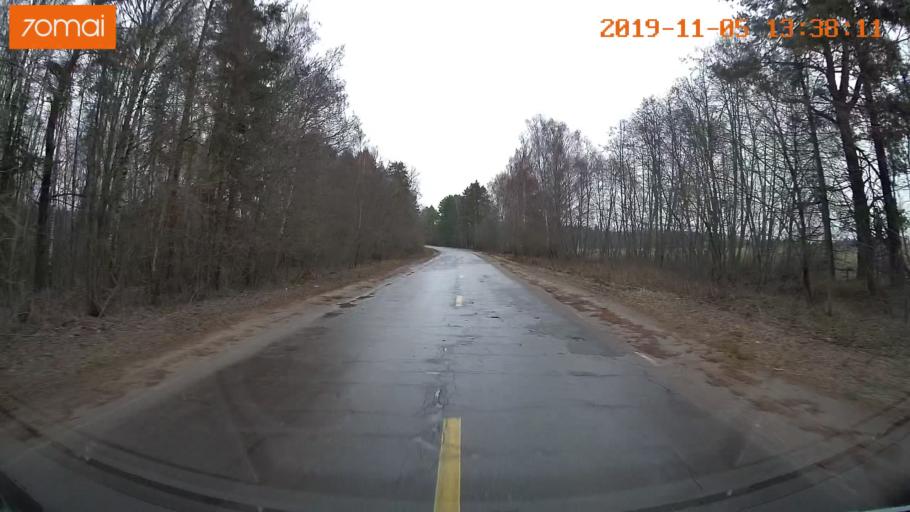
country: RU
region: Ivanovo
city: Shuya
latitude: 56.9295
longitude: 41.3848
